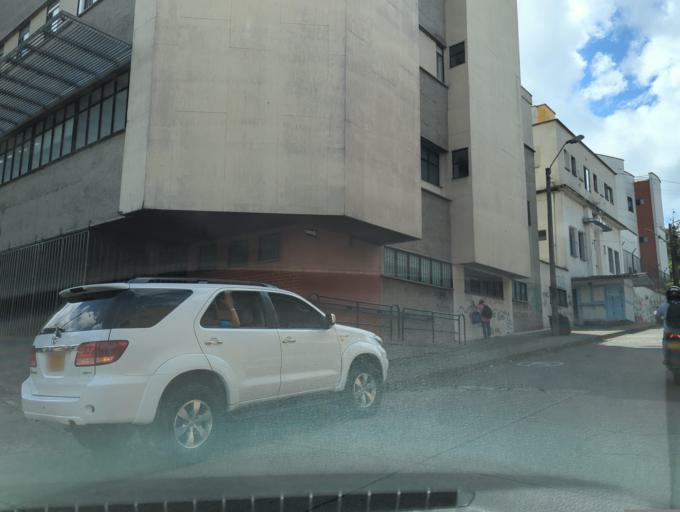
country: CO
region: Risaralda
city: Pereira
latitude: 4.8187
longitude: -75.6997
